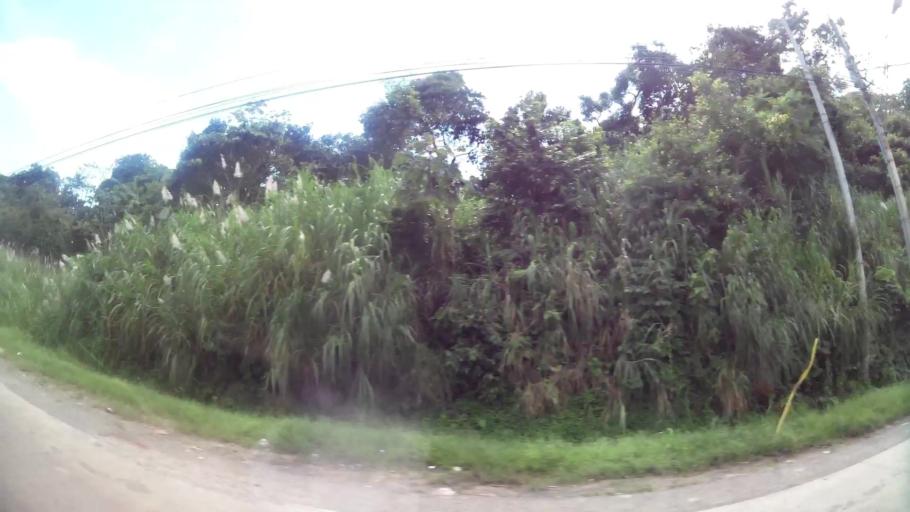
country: PA
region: Panama
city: Las Cumbres
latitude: 9.0396
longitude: -79.5465
